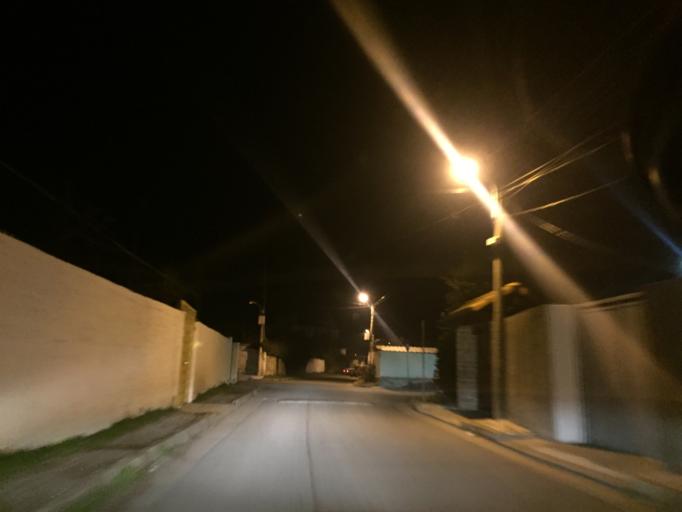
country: AL
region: Shkoder
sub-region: Rrethi i Shkodres
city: Shkoder
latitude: 42.0684
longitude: 19.4994
